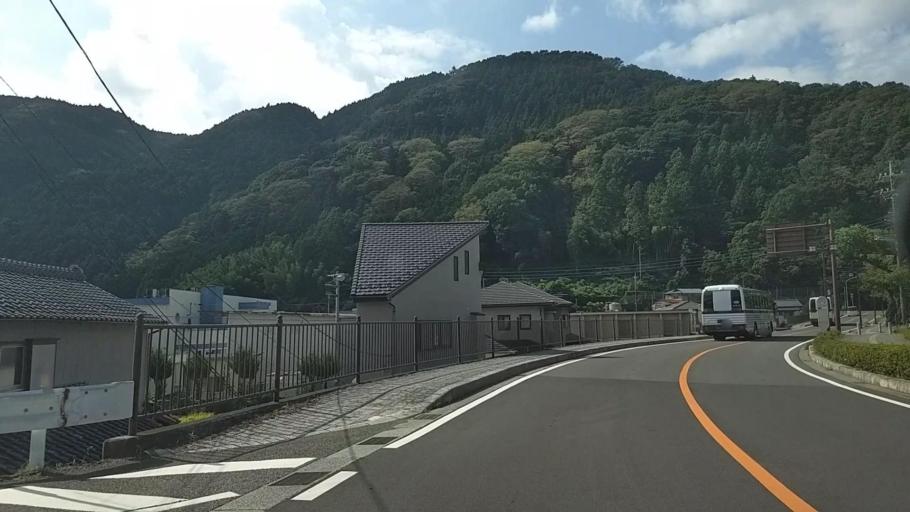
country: JP
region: Shizuoka
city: Fujinomiya
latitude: 35.3649
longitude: 138.4498
